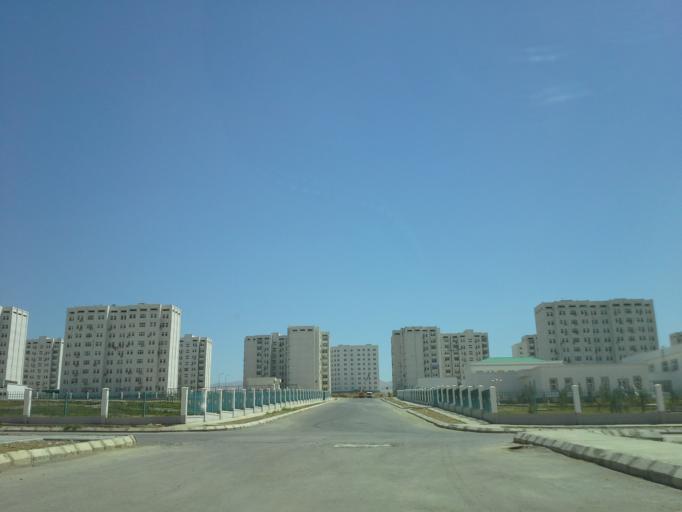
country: TM
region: Ahal
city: Ashgabat
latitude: 37.8989
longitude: 58.4178
